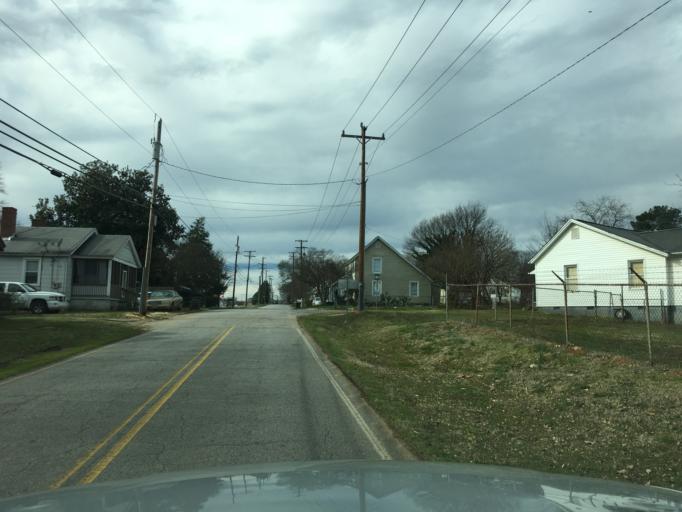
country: US
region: South Carolina
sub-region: Greenville County
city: Greer
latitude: 34.9306
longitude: -82.2154
